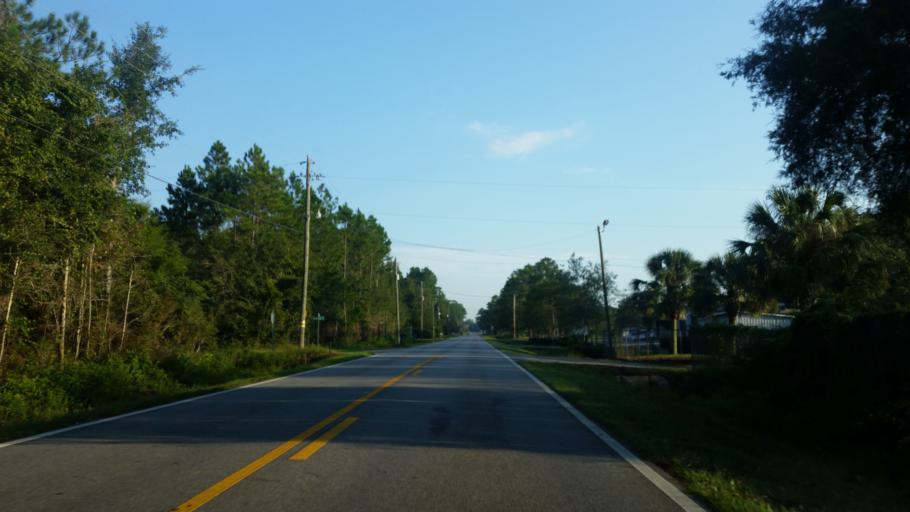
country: US
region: Florida
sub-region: Santa Rosa County
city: East Milton
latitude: 30.6144
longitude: -87.0215
